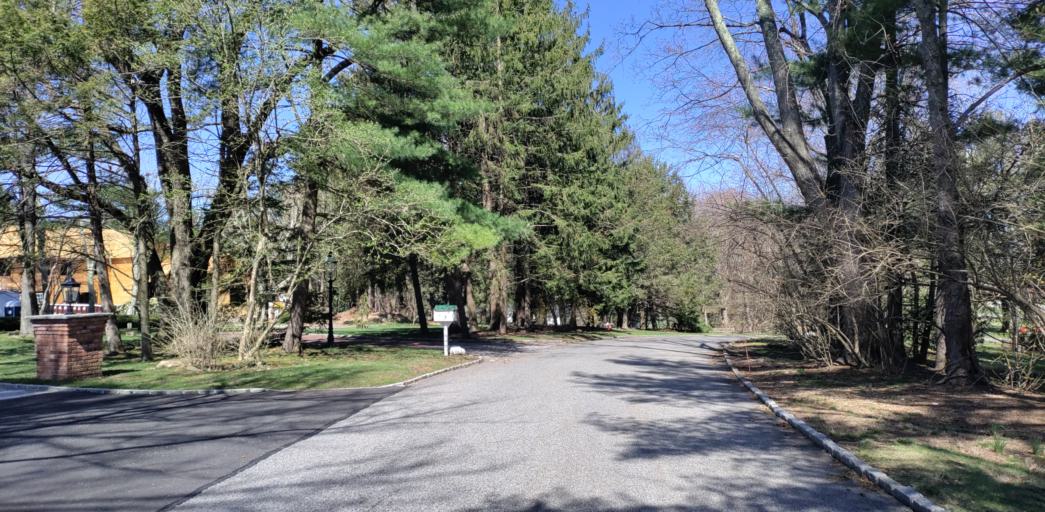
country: US
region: New York
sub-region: Nassau County
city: Old Brookville
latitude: 40.8280
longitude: -73.6024
